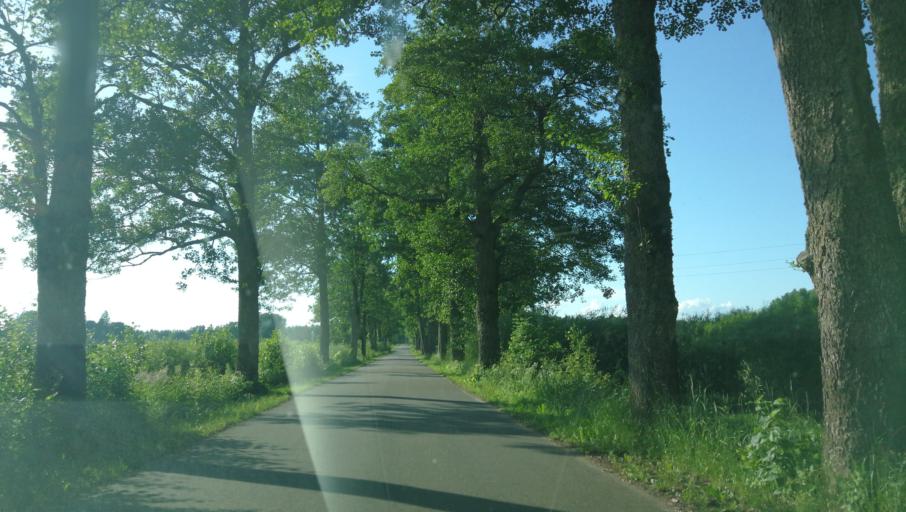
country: LV
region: Pargaujas
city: Stalbe
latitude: 57.3540
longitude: 25.0931
